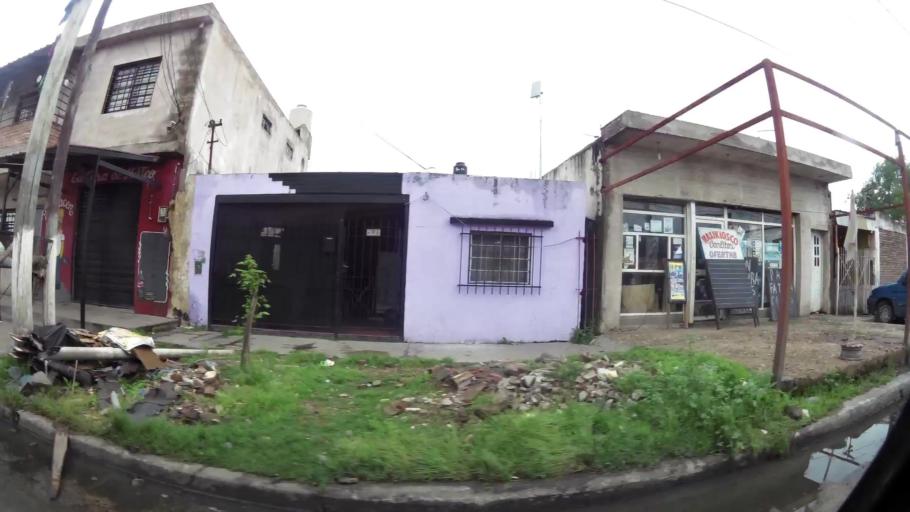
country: AR
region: Buenos Aires
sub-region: Partido de Lanus
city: Lanus
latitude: -34.7236
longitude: -58.3741
